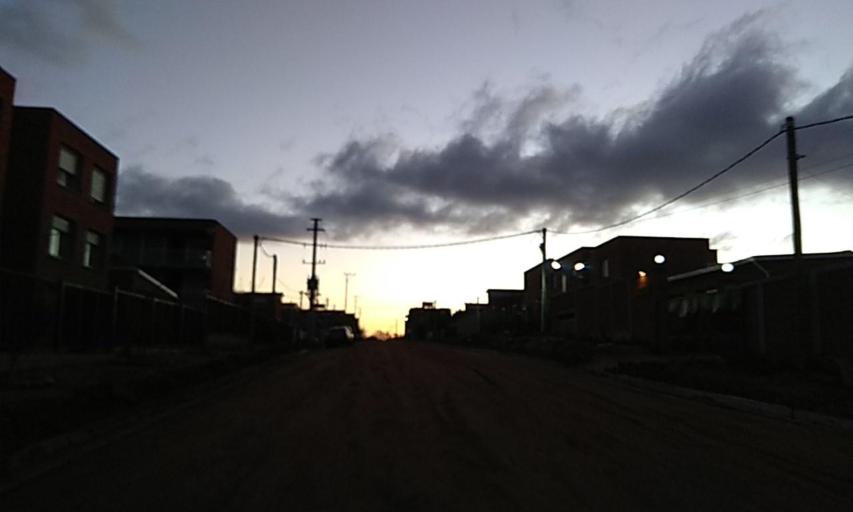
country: UY
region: Florida
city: Florida
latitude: -34.1082
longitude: -56.2066
